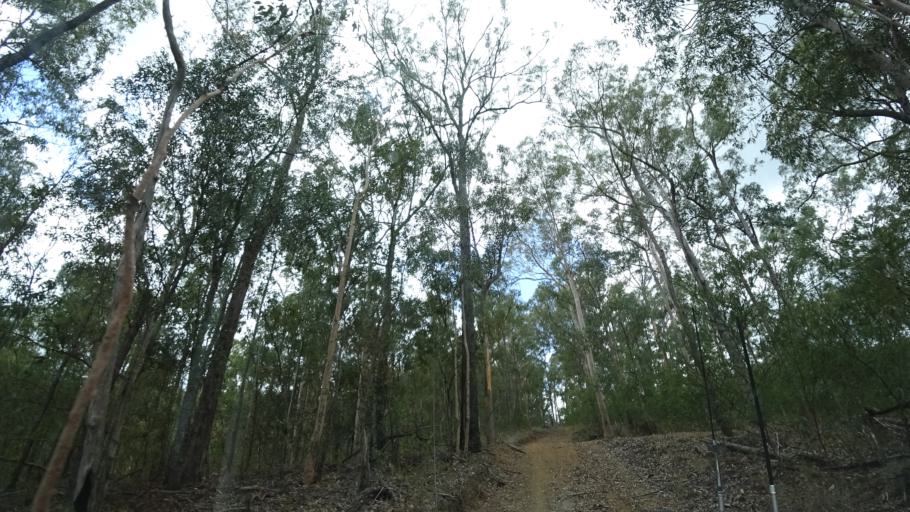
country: AU
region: Queensland
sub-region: Moreton Bay
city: Highvale
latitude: -27.4119
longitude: 152.7387
